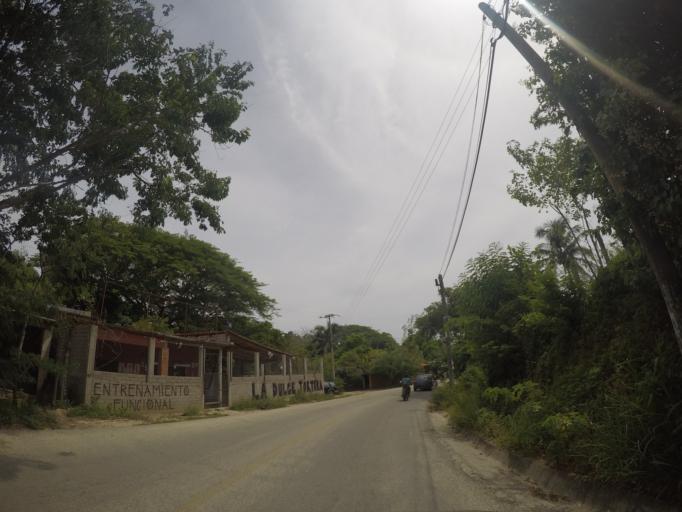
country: MX
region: Oaxaca
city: San Pedro Pochutla
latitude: 15.6633
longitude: -96.5048
